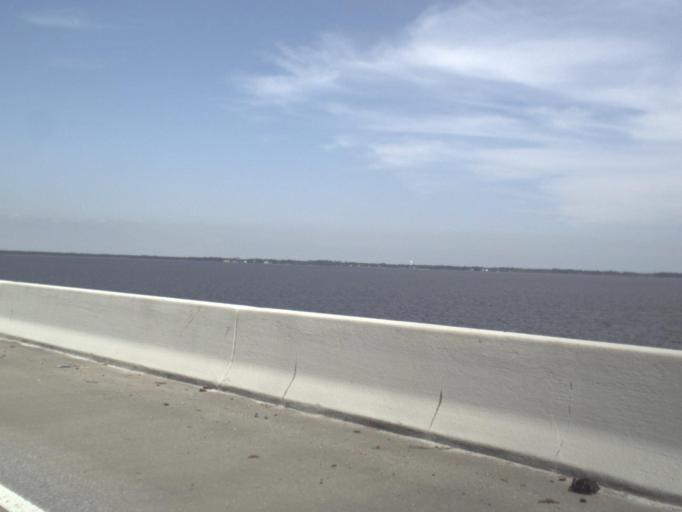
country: US
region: Florida
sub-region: Escambia County
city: Ferry Pass
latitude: 30.5112
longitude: -87.1548
